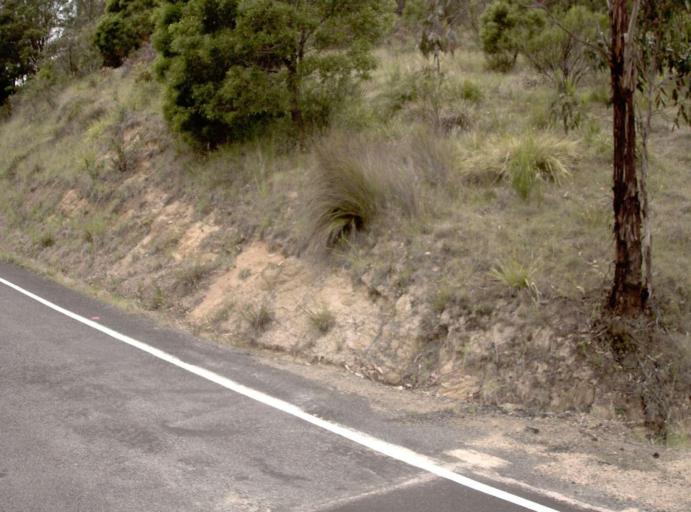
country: AU
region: New South Wales
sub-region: Bombala
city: Bombala
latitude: -37.2385
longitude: 149.2649
